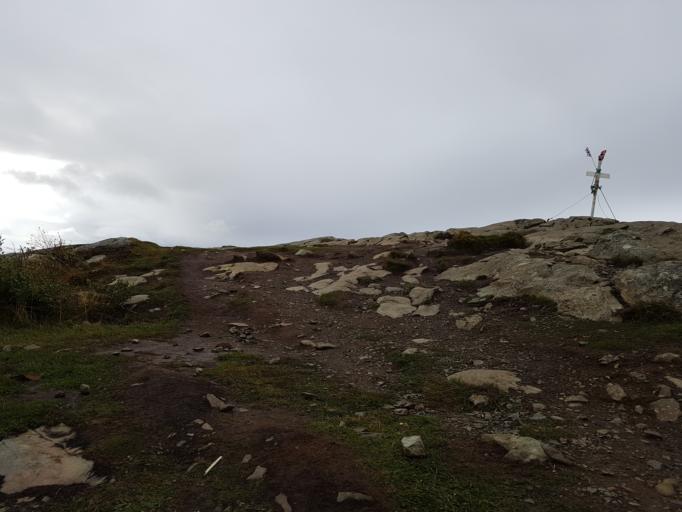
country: NO
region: Sor-Trondelag
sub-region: Melhus
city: Melhus
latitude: 63.4023
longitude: 10.2012
